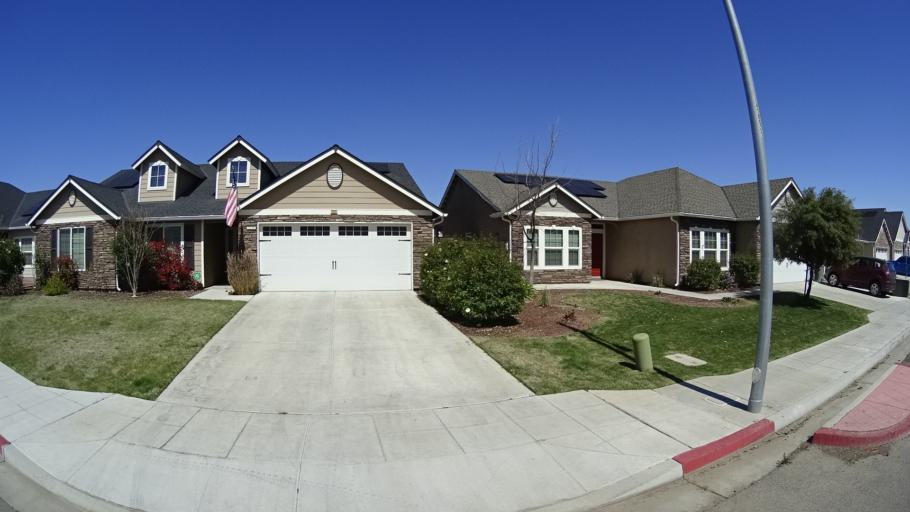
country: US
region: California
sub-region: Fresno County
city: West Park
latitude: 36.7745
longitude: -119.8881
